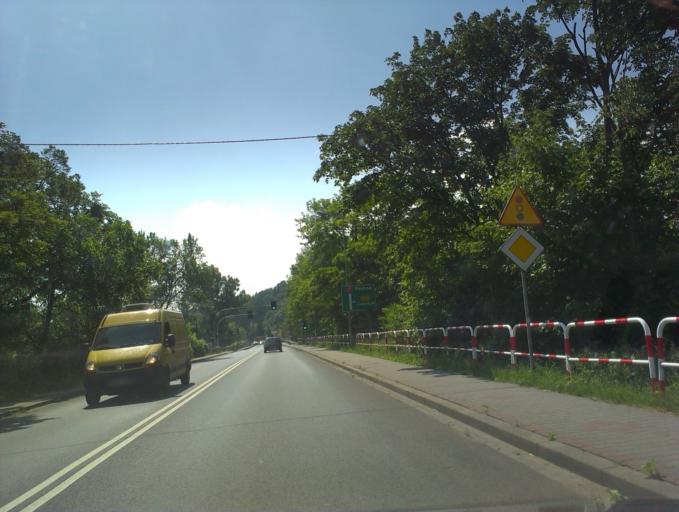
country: PL
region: Greater Poland Voivodeship
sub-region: Powiat pilski
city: Ujscie
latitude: 53.0559
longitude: 16.7297
